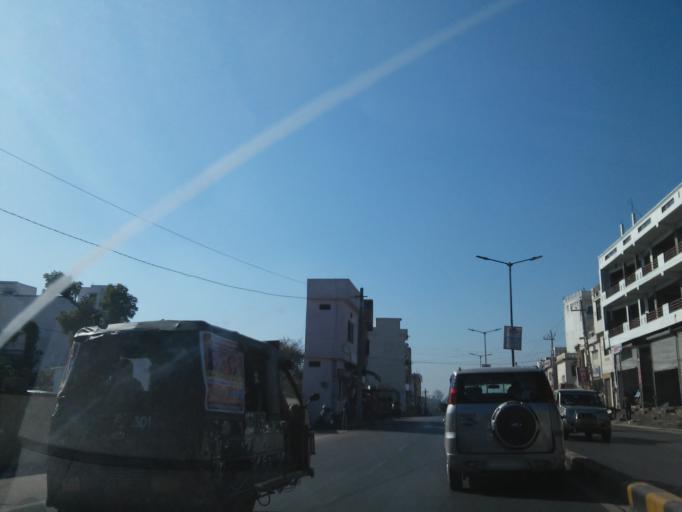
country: IN
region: Rajasthan
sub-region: Udaipur
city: Udaipur
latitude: 24.5470
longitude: 73.6875
